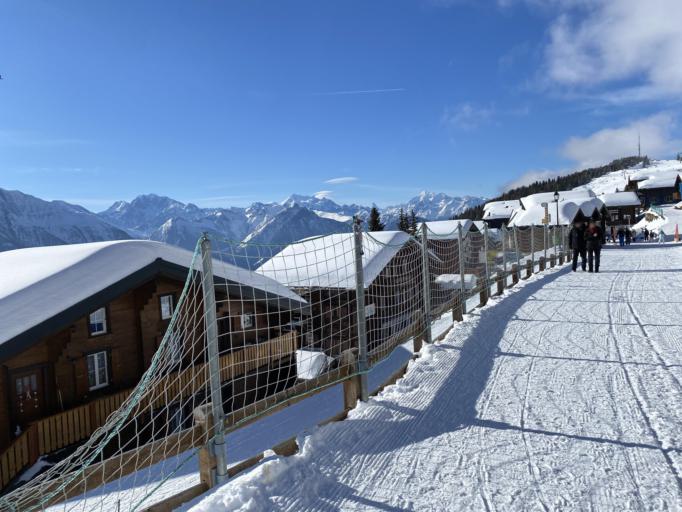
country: CH
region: Valais
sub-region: Goms District
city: Fiesch
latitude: 46.3912
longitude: 8.0642
